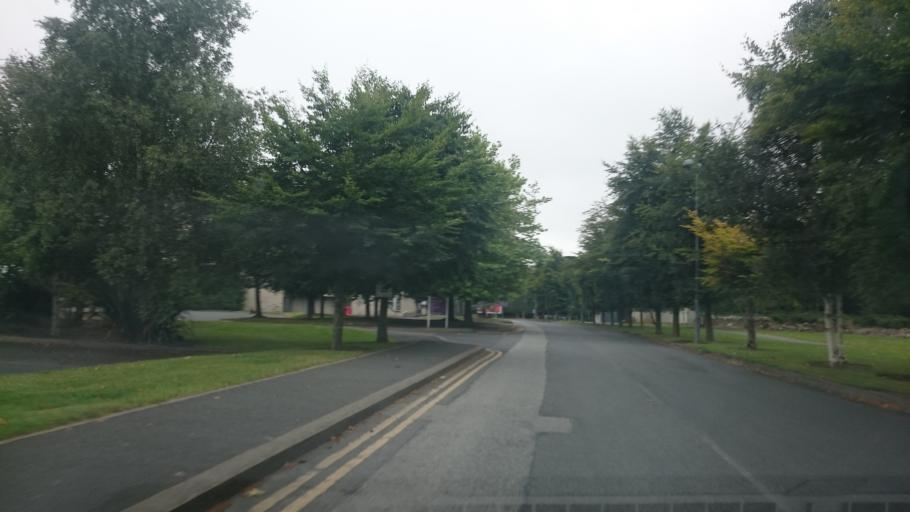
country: IE
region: Leinster
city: Foxrock
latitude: 53.2680
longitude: -6.1948
